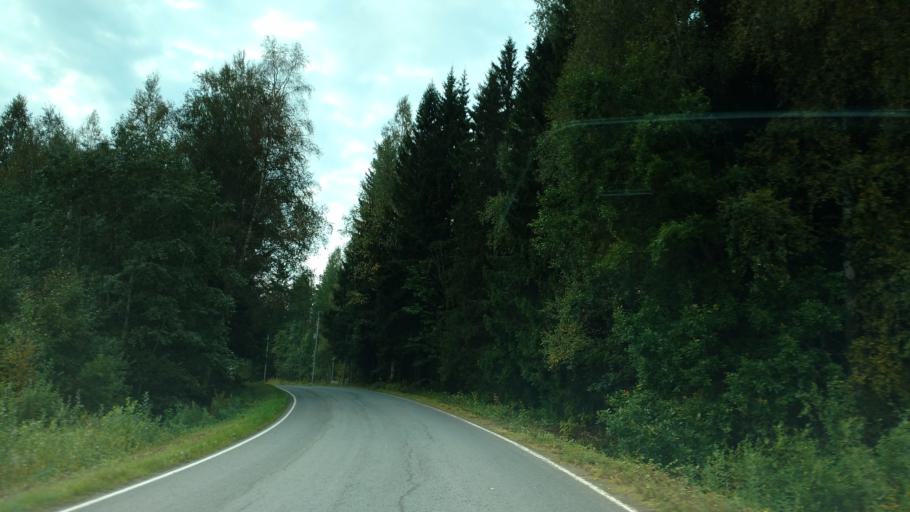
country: FI
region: Varsinais-Suomi
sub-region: Loimaa
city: Koski Tl
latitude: 60.7360
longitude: 23.1913
